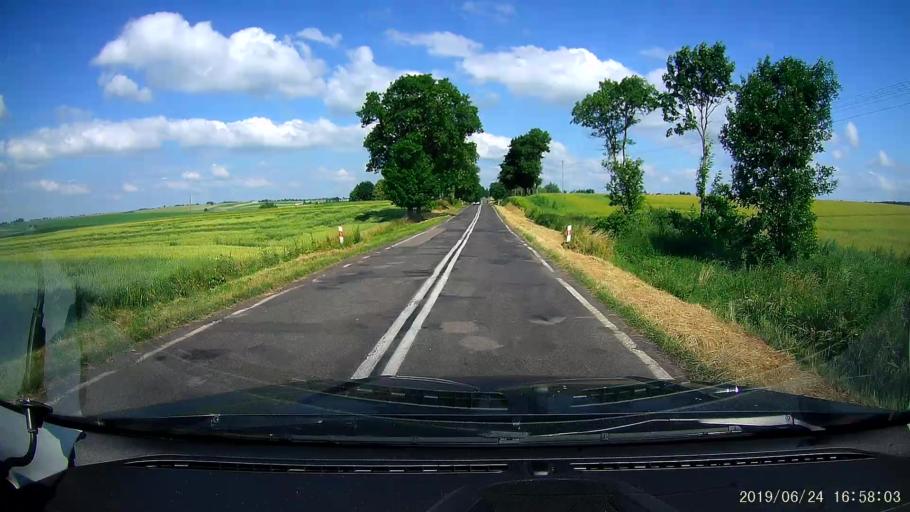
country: PL
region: Lublin Voivodeship
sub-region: Powiat tomaszowski
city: Telatyn
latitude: 50.5257
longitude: 23.8713
